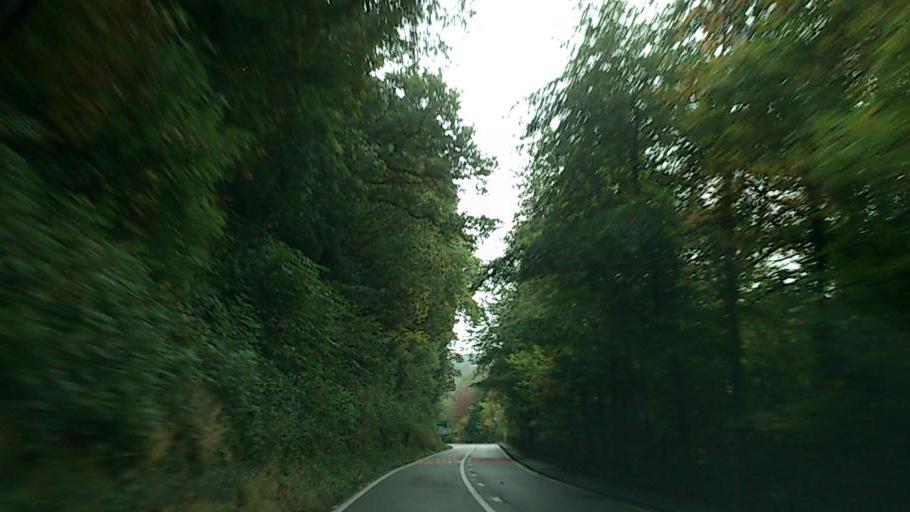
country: GB
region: Wales
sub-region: Sir Powys
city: Llanfyllin
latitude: 52.6499
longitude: -3.3315
